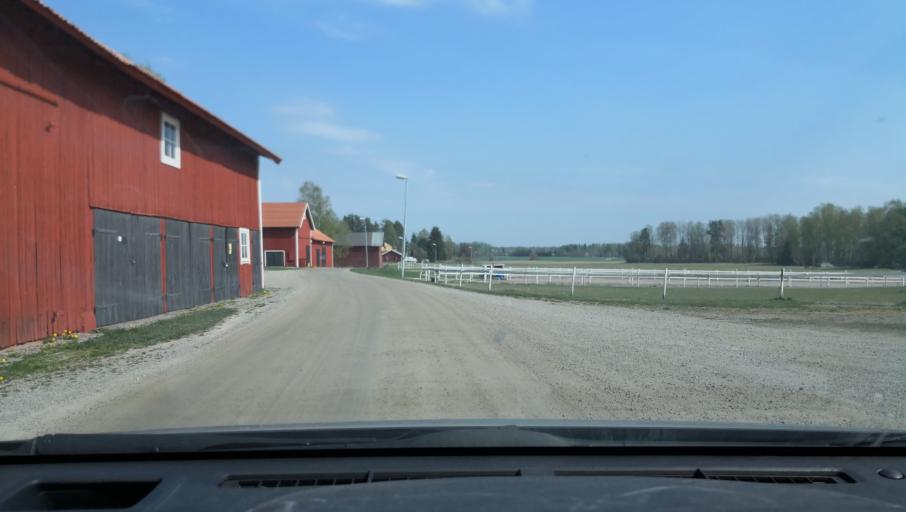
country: SE
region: Vaestmanland
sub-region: Vasteras
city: Skultuna
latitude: 59.7536
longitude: 16.4376
